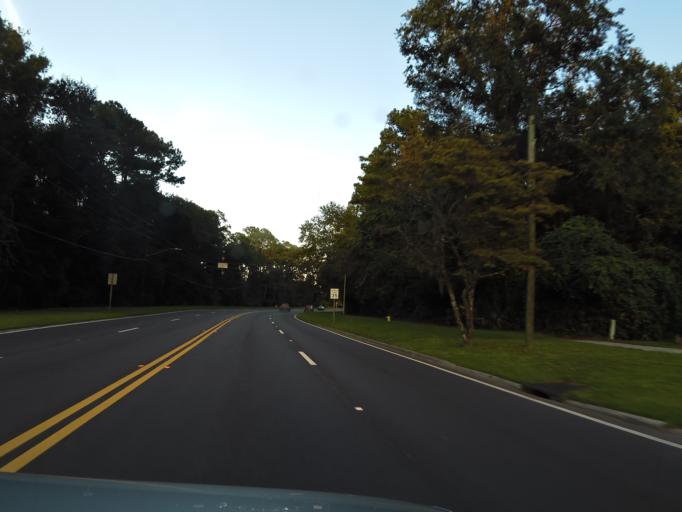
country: US
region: Georgia
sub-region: Camden County
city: Kingsland
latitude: 30.8010
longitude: -81.6836
